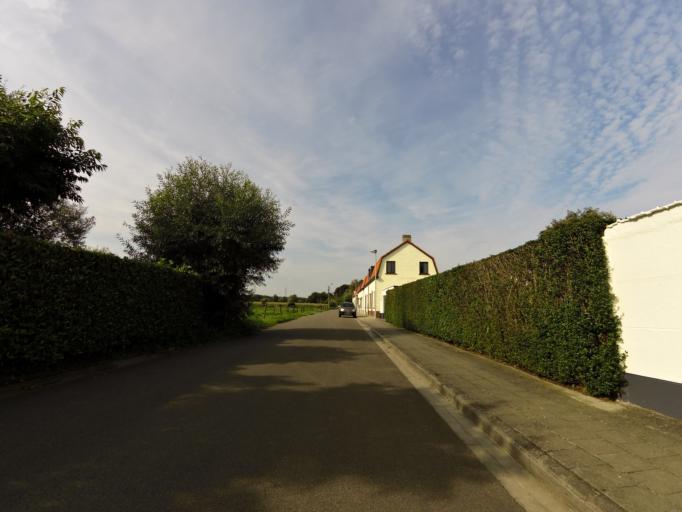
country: BE
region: Flanders
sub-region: Provincie West-Vlaanderen
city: Sint-Kruis
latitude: 51.2177
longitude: 3.2708
